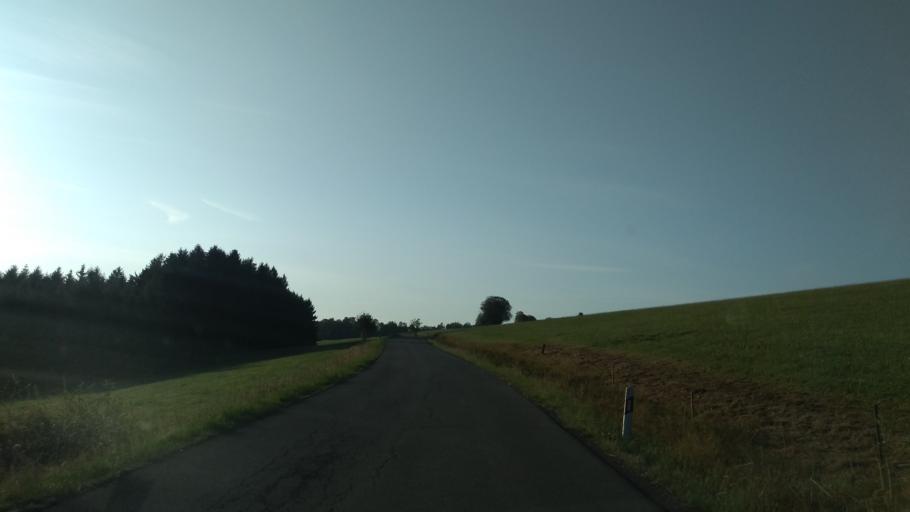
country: DE
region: North Rhine-Westphalia
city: Kierspe
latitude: 51.0815
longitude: 7.5930
